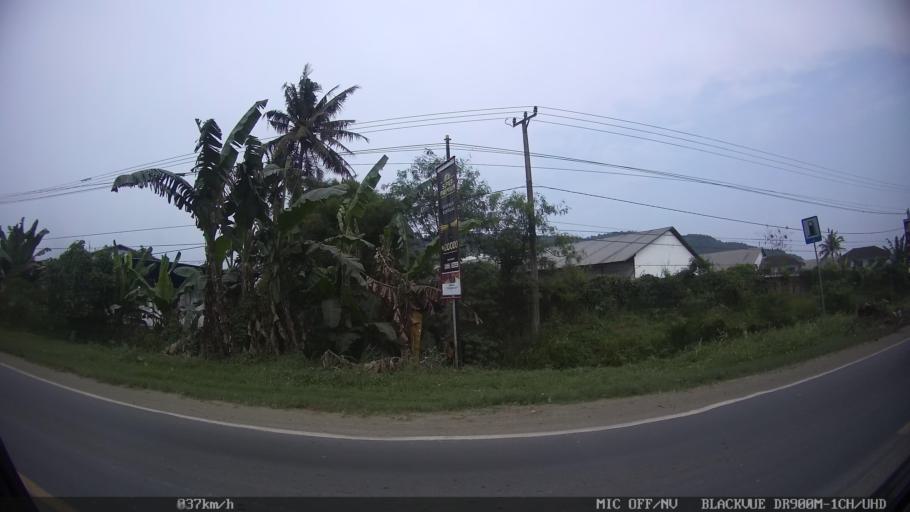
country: ID
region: Lampung
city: Panjang
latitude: -5.4341
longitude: 105.3246
